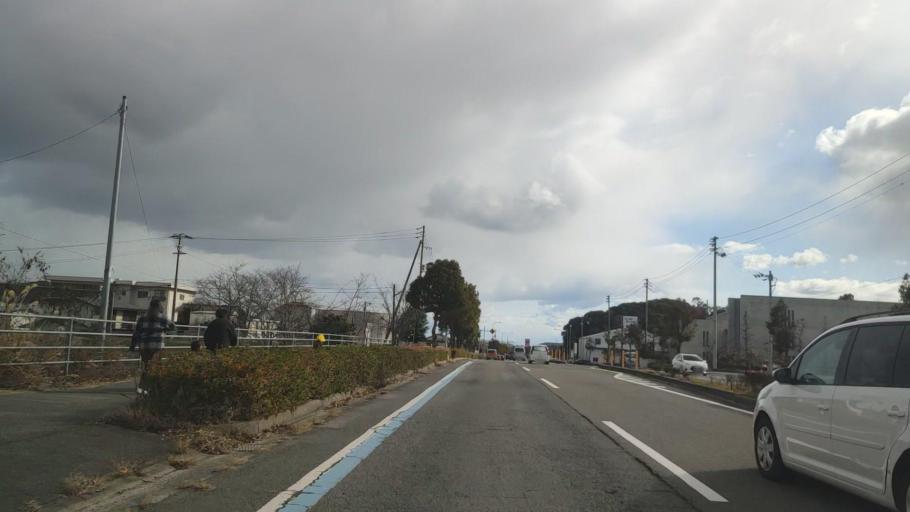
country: JP
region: Ehime
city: Hojo
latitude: 34.0622
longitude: 132.9589
